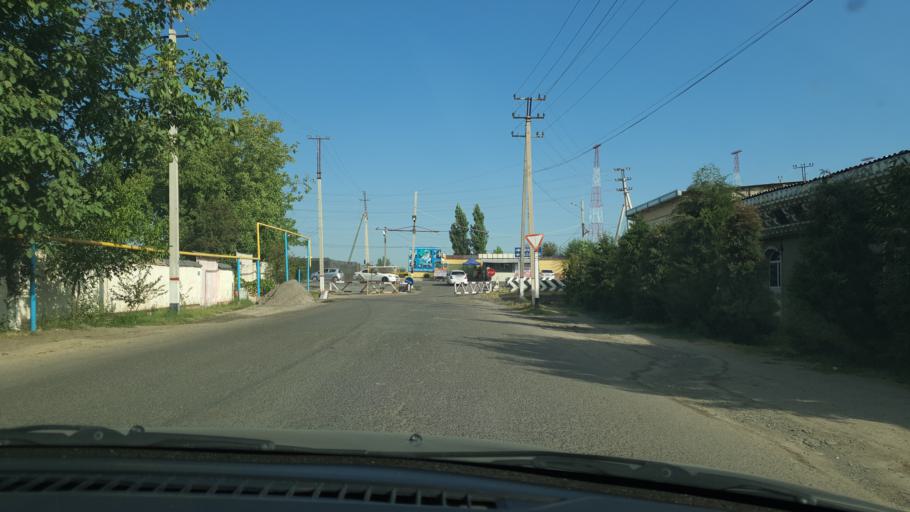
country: UZ
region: Toshkent
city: Urtaowul
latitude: 41.2072
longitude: 69.1484
